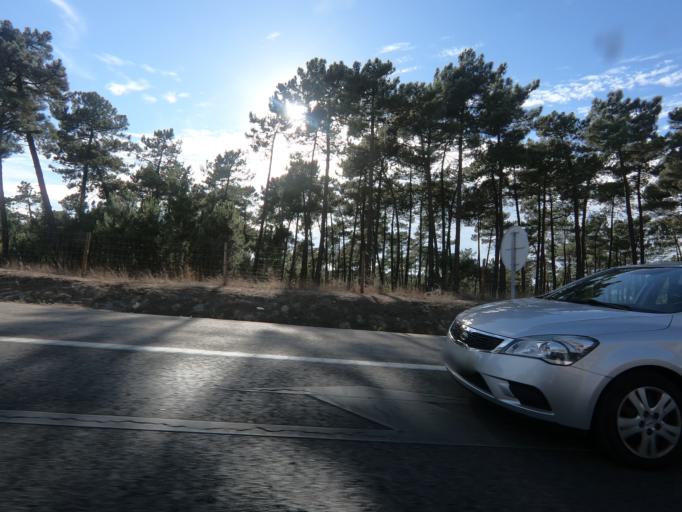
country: PT
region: Setubal
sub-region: Barreiro
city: Santo Antonio da Charneca
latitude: 38.6109
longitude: -9.0254
